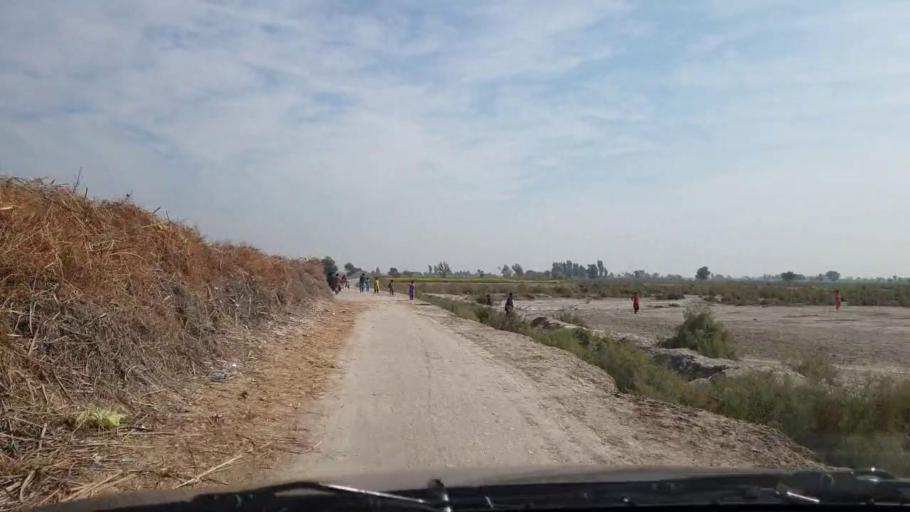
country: PK
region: Sindh
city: Jam Sahib
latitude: 26.2691
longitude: 68.7080
